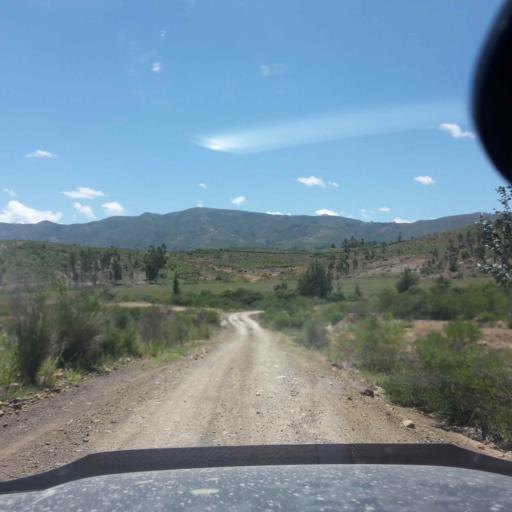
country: BO
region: Cochabamba
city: Totora
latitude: -17.7700
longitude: -65.2633
